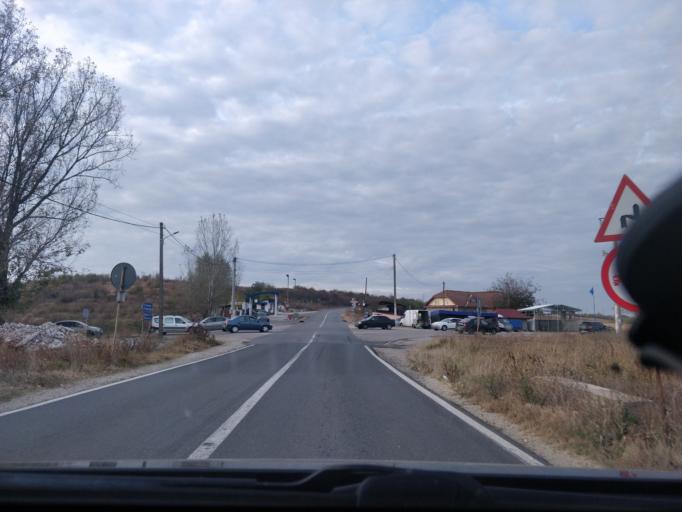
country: RO
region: Giurgiu
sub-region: Comuna Crevedia Mare
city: Crevedia Mare
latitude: 44.4180
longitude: 25.6336
